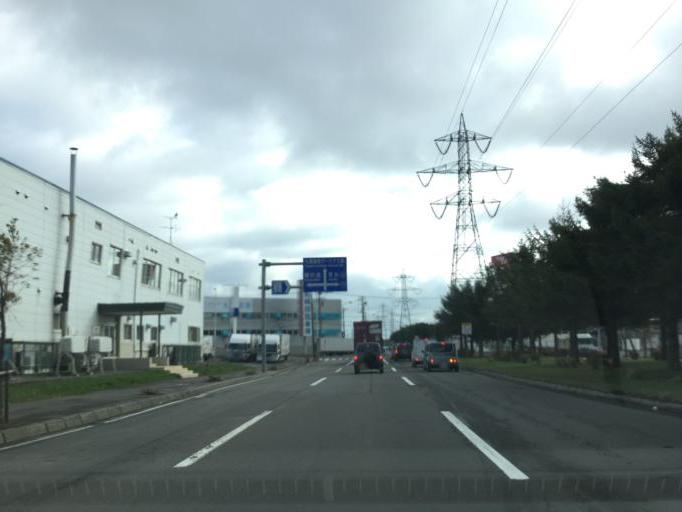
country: JP
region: Hokkaido
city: Sapporo
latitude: 43.0377
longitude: 141.4437
